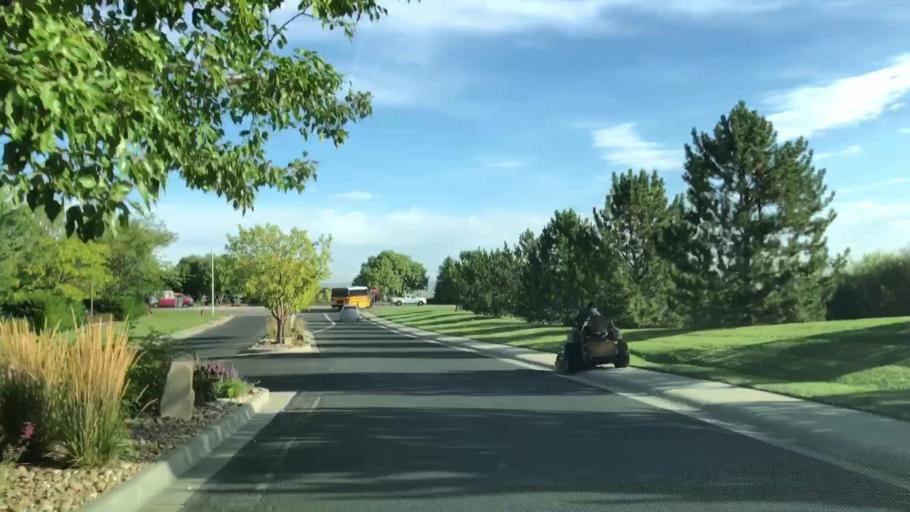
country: US
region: Colorado
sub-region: Weld County
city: Windsor
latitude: 40.4783
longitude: -104.9738
